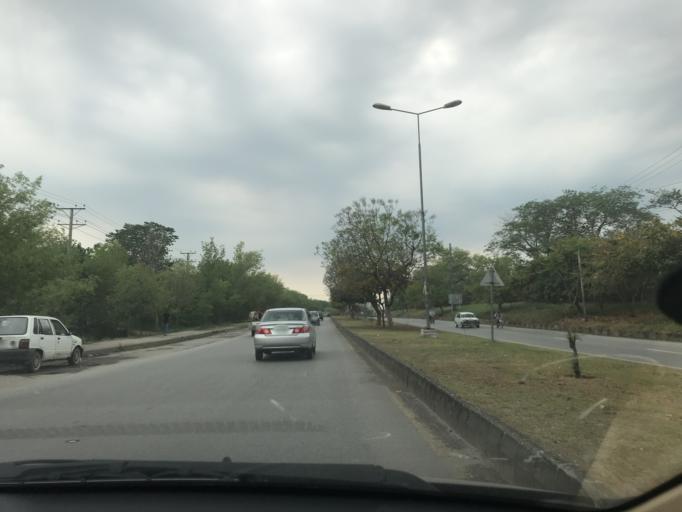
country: PK
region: Islamabad
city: Islamabad
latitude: 33.6882
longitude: 73.1207
